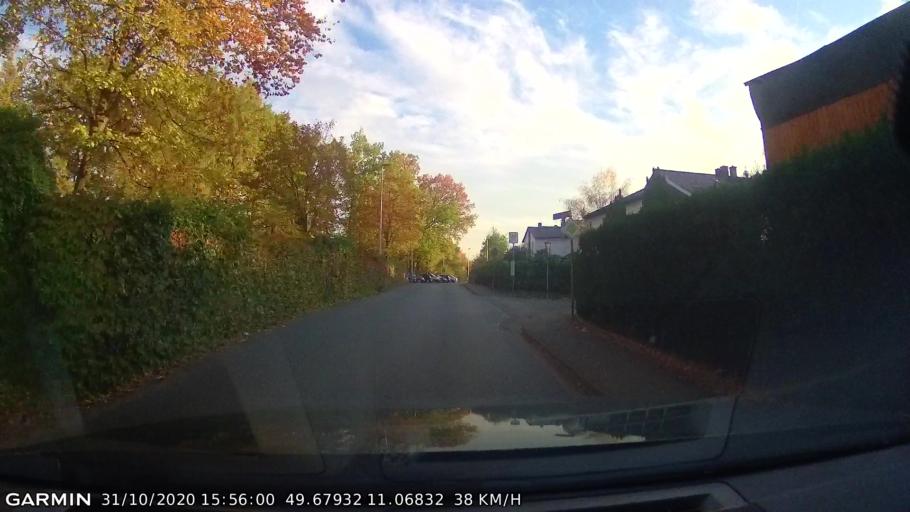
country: DE
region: Bavaria
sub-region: Upper Franconia
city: Poxdorf
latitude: 49.6793
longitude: 11.0684
